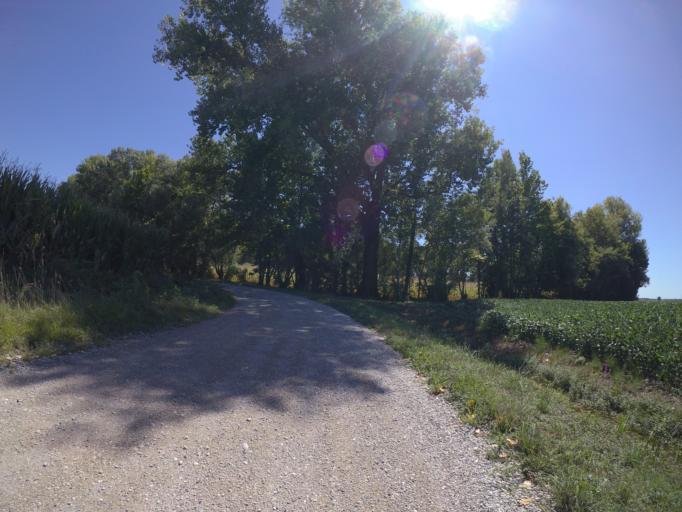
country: IT
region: Friuli Venezia Giulia
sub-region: Provincia di Udine
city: Rivignano
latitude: 45.8730
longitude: 13.0203
